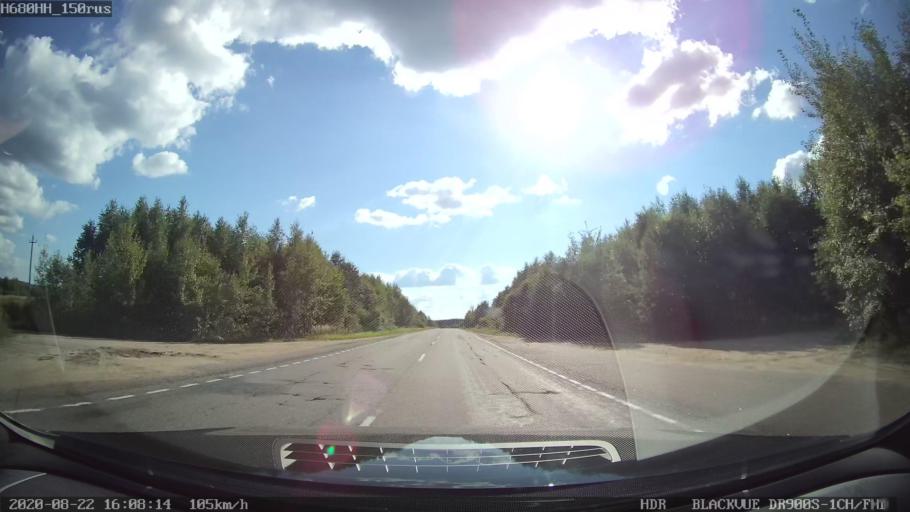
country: RU
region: Tverskaya
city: Rameshki
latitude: 57.5431
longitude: 36.3010
